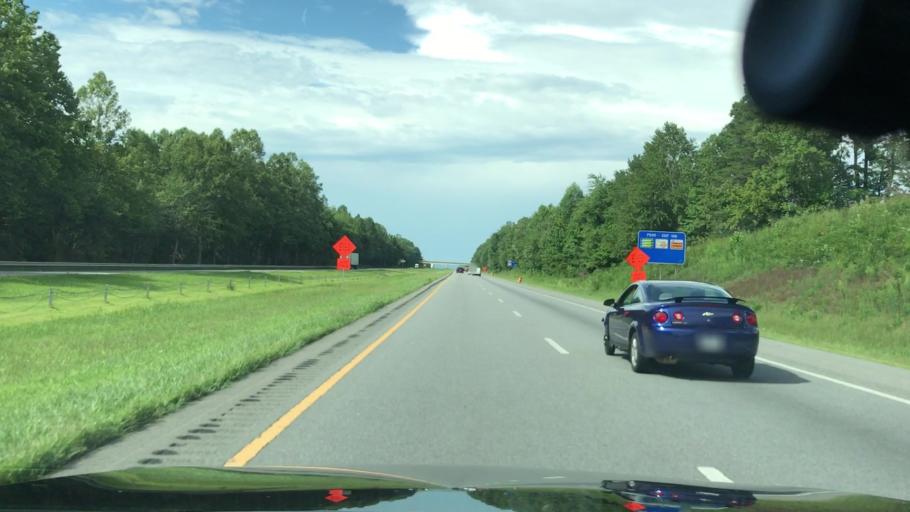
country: US
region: North Carolina
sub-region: Surry County
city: Dobson
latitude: 36.4709
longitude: -80.7553
